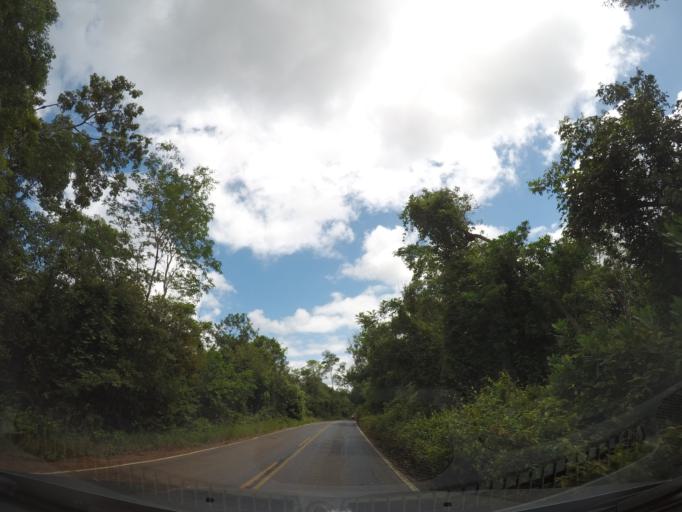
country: BR
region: Bahia
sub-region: Iraquara
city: Iraquara
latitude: -12.4902
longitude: -41.3622
